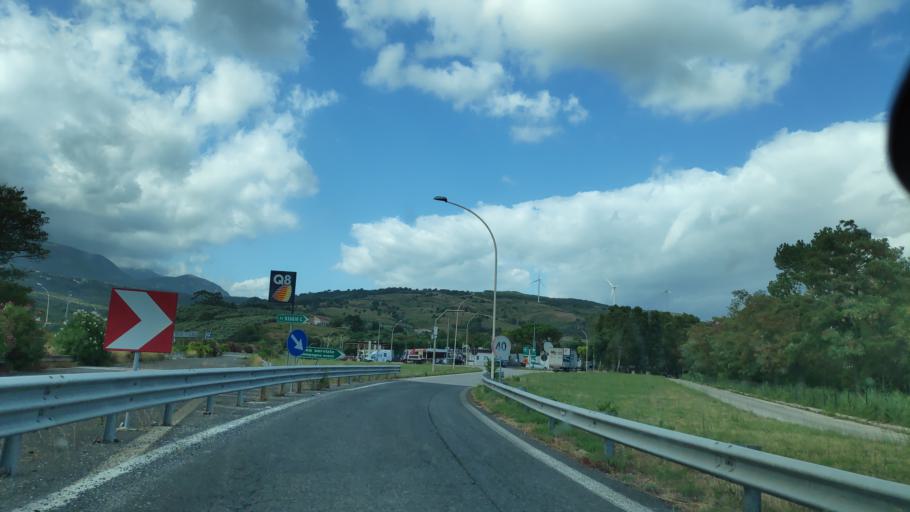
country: IT
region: Campania
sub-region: Provincia di Salerno
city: Serre
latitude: 40.6224
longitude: 15.1819
